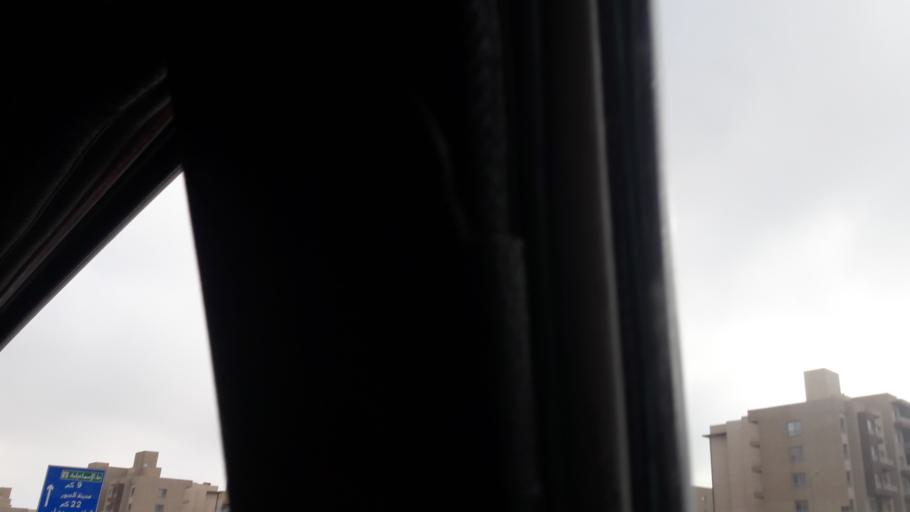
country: EG
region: Muhafazat al Qalyubiyah
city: Al Khankah
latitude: 30.1113
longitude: 31.5844
